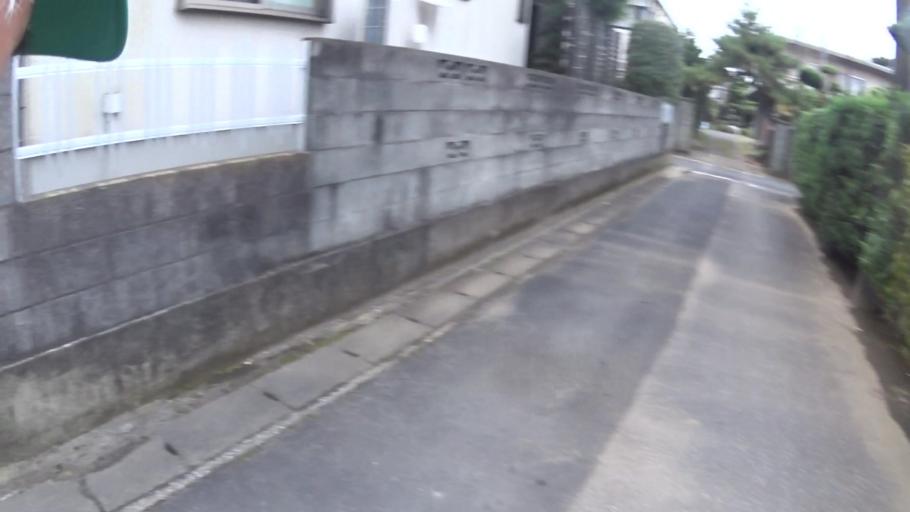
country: JP
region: Saitama
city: Yashio-shi
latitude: 35.8352
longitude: 139.8475
